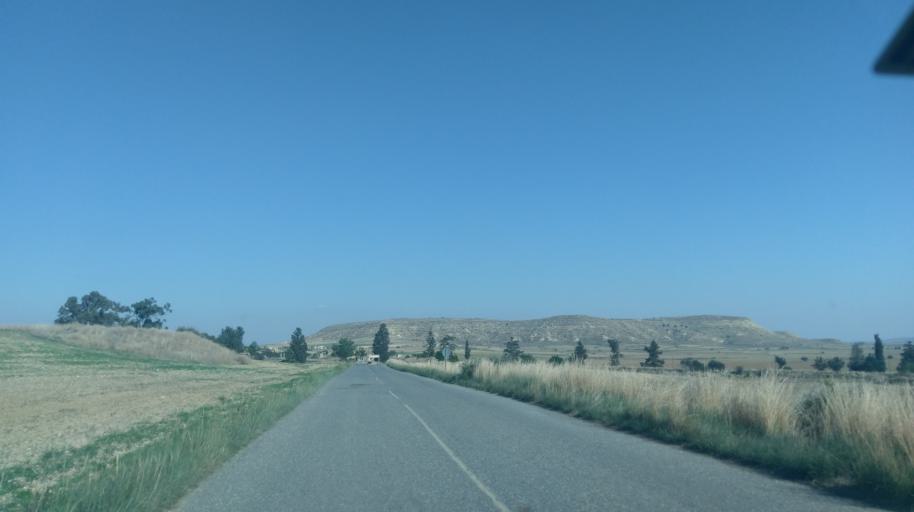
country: CY
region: Larnaka
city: Athienou
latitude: 35.0726
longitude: 33.4883
